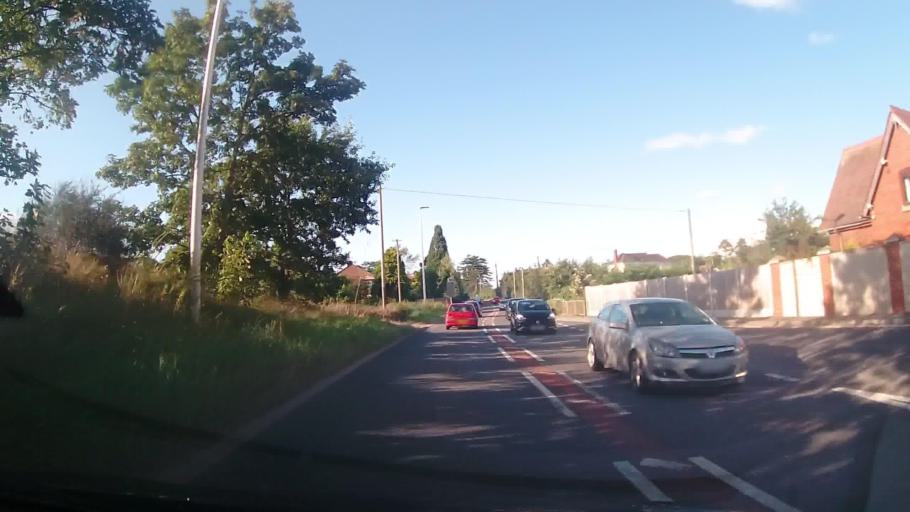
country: GB
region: England
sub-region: Shropshire
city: Bayston Hill
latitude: 52.6718
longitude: -2.7612
